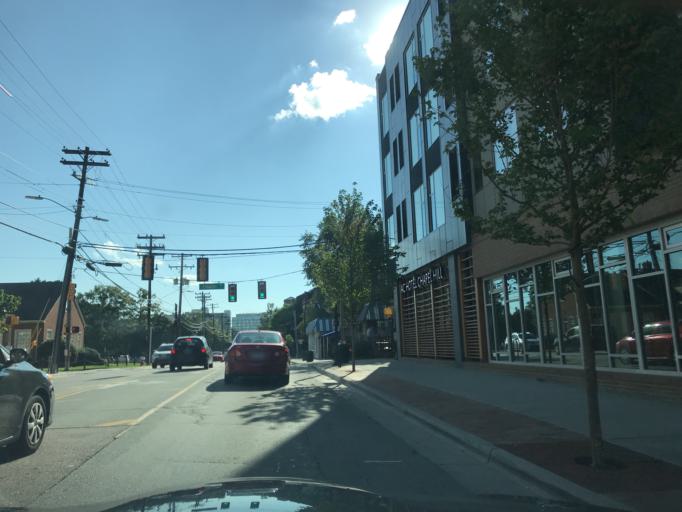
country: US
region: North Carolina
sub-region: Orange County
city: Chapel Hill
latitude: 35.9133
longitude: -79.0584
